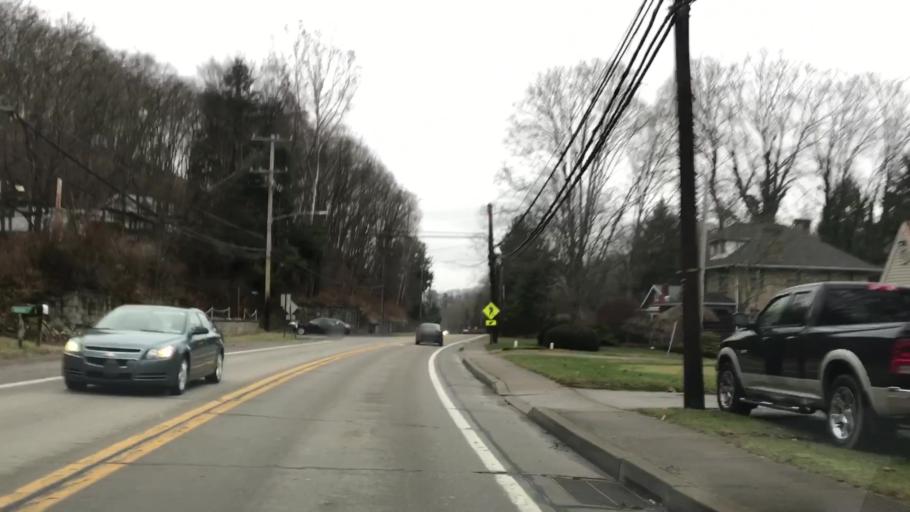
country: US
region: Pennsylvania
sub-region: Allegheny County
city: Leetsdale
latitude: 40.5460
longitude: -80.2185
